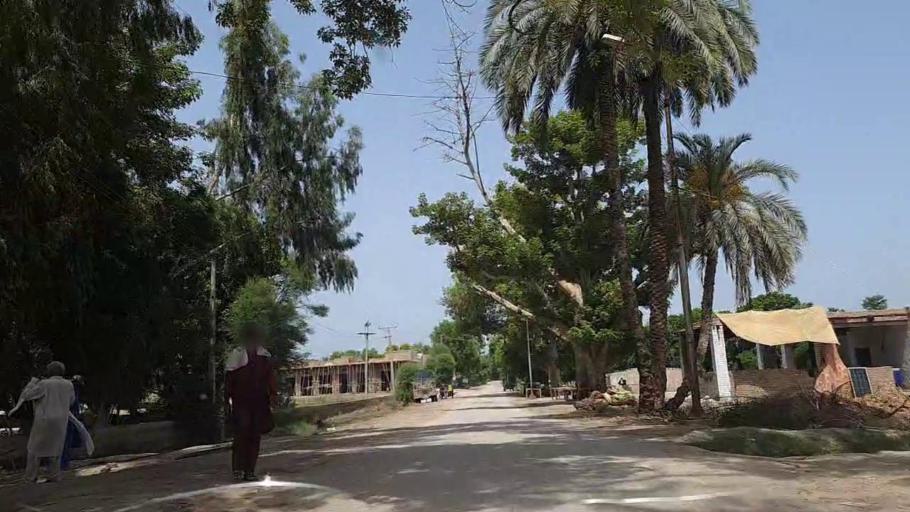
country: PK
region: Sindh
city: Tharu Shah
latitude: 27.0144
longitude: 68.1281
